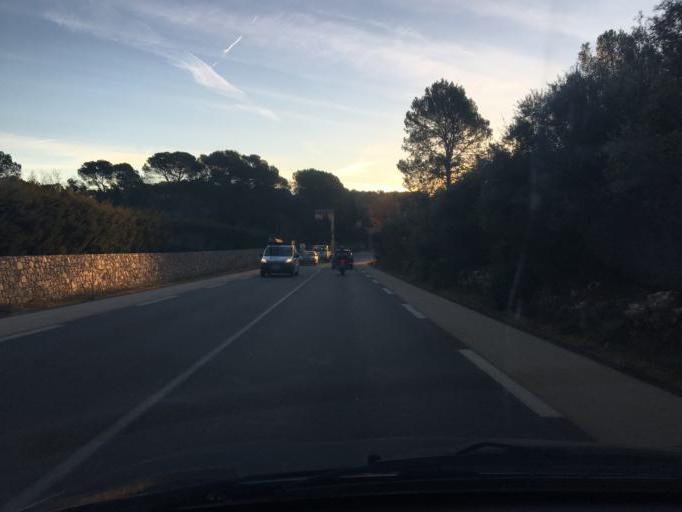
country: FR
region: Provence-Alpes-Cote d'Azur
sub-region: Departement du Var
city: Taradeau
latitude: 43.4645
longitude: 6.3980
